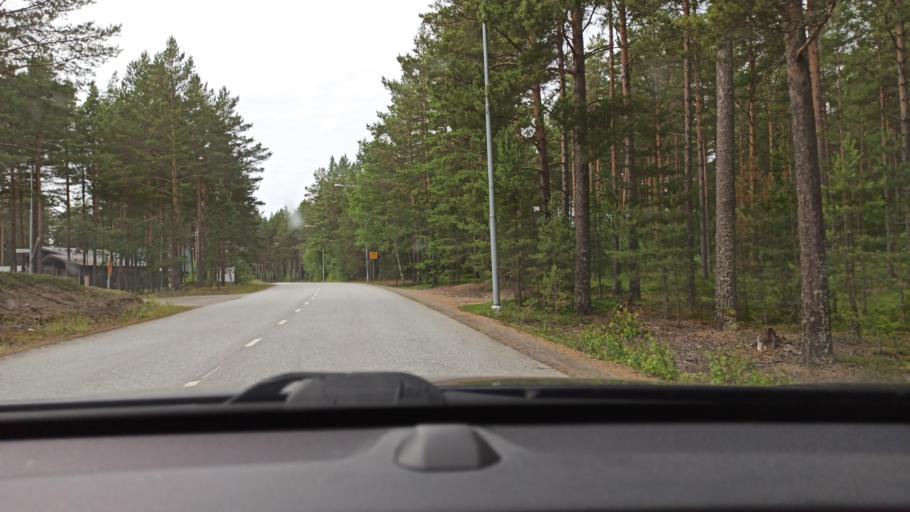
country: FI
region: Satakunta
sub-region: Pori
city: Luvia
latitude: 61.5742
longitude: 21.5275
